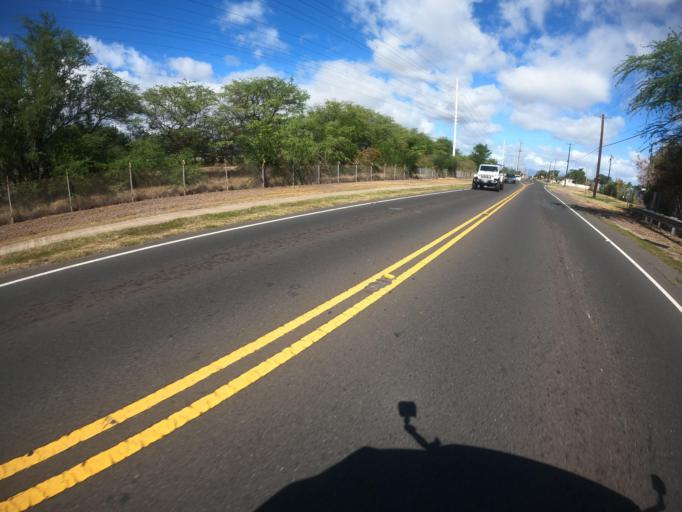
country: US
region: Hawaii
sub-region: Honolulu County
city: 'Ewa Villages
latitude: 21.3255
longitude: -158.0653
